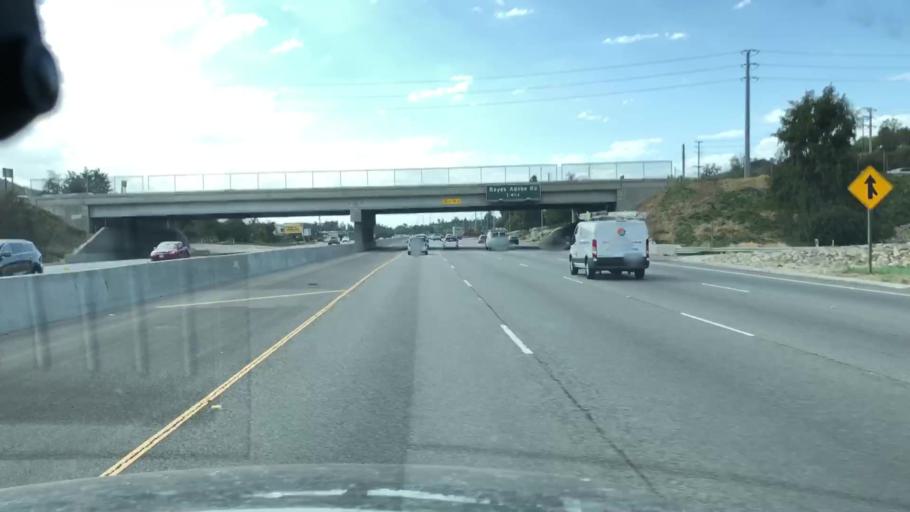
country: US
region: California
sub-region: Los Angeles County
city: Agoura Hills
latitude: 34.1461
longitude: -118.7599
